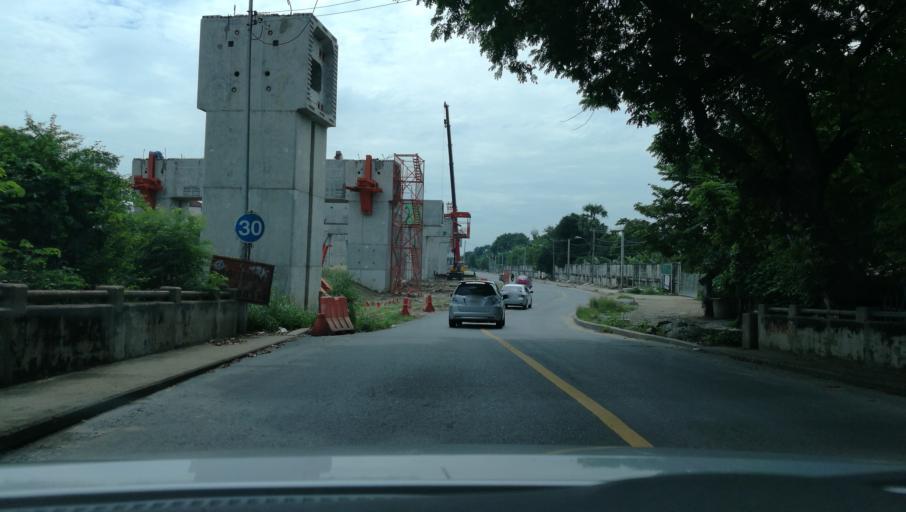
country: TH
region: Bangkok
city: Bang Sue
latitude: 13.7974
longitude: 100.5371
